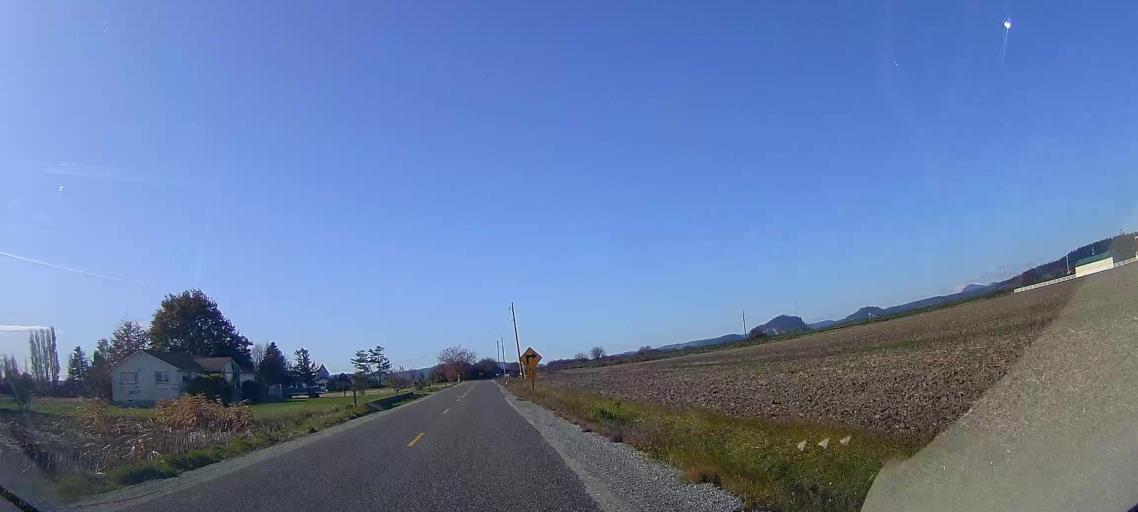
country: US
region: Washington
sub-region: Snohomish County
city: Stanwood
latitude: 48.3411
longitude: -122.4367
